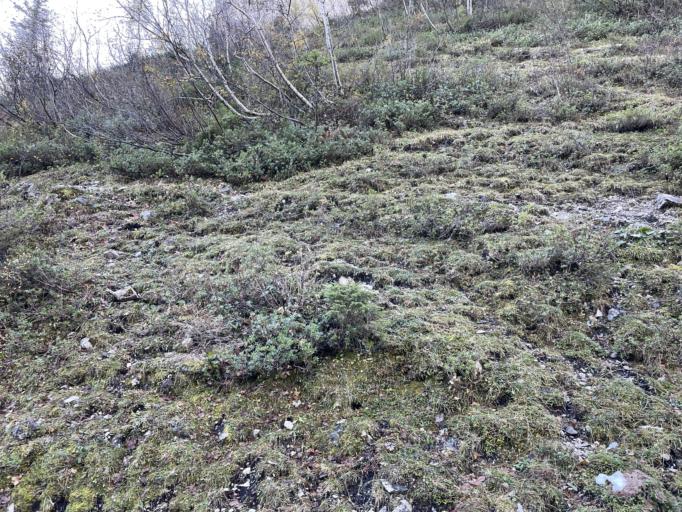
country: AT
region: Tyrol
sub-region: Politischer Bezirk Innsbruck Land
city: Gnadenwald
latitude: 47.3896
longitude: 11.5400
